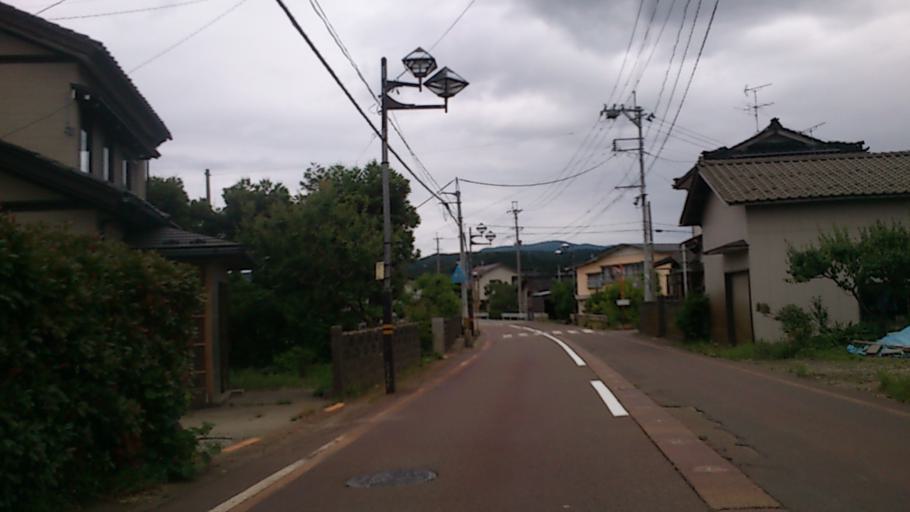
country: JP
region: Yamagata
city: Tsuruoka
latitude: 38.7912
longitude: 139.9790
